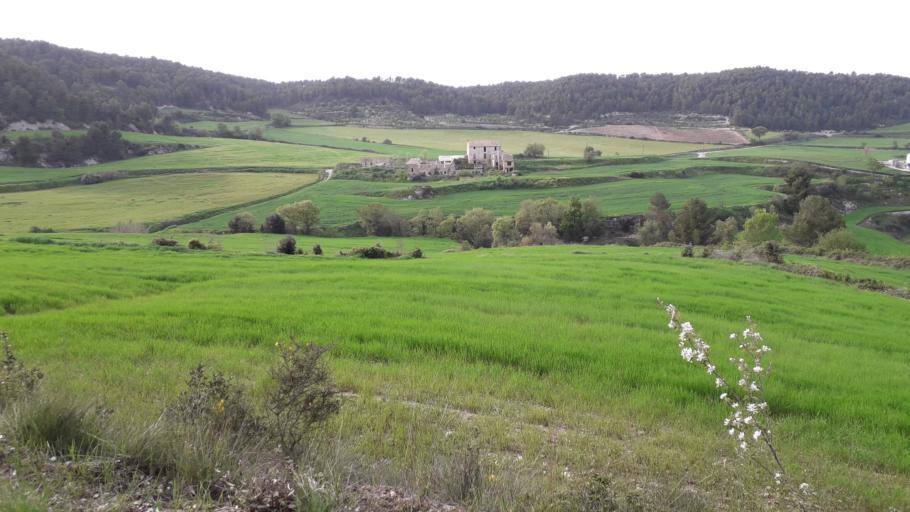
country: ES
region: Catalonia
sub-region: Provincia de Barcelona
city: Orpi
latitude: 41.5526
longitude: 1.5563
